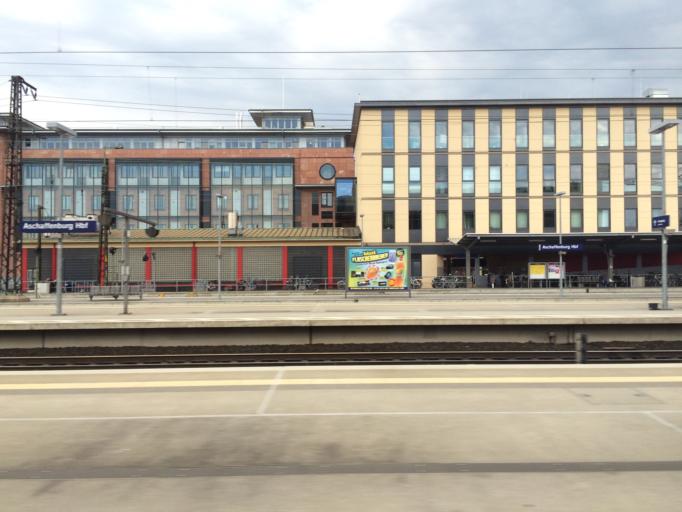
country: DE
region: Bavaria
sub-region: Regierungsbezirk Unterfranken
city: Aschaffenburg
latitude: 49.9806
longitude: 9.1450
